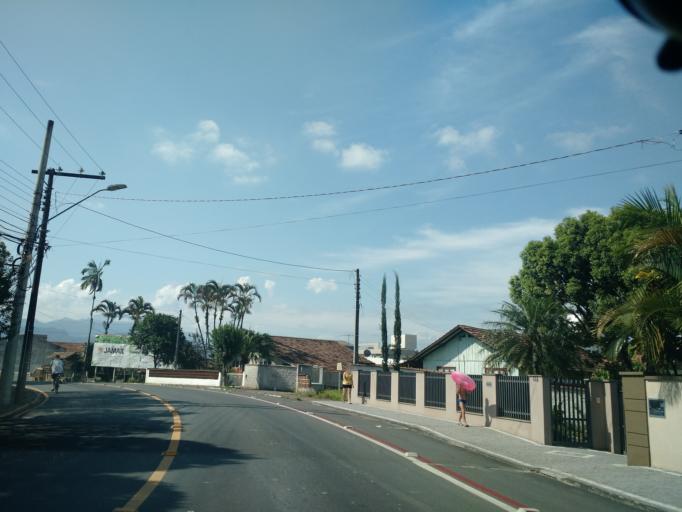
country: BR
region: Santa Catarina
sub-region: Jaragua Do Sul
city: Jaragua do Sul
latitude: -26.4808
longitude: -49.1034
